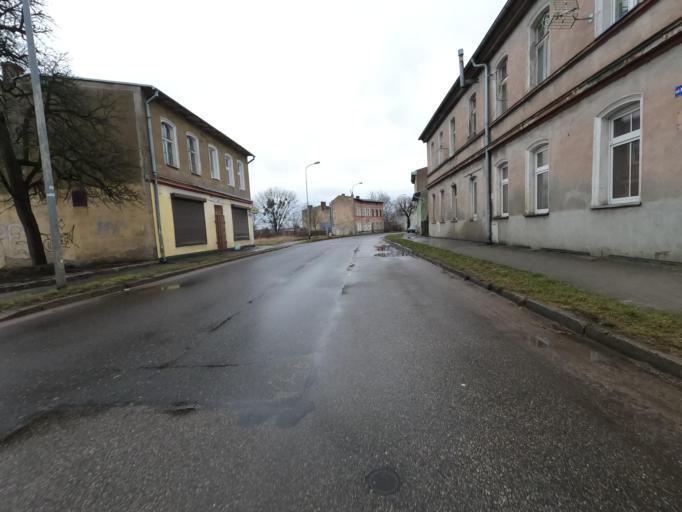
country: PL
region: Greater Poland Voivodeship
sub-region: Powiat pilski
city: Pila
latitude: 53.1432
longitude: 16.7570
